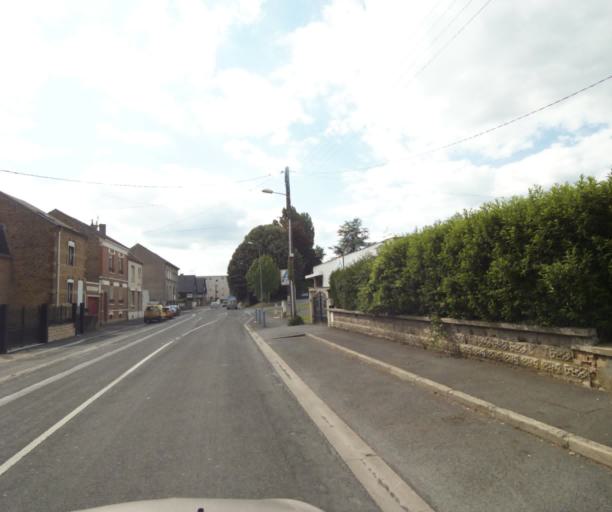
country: FR
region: Champagne-Ardenne
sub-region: Departement des Ardennes
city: Charleville-Mezieres
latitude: 49.7586
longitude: 4.7313
